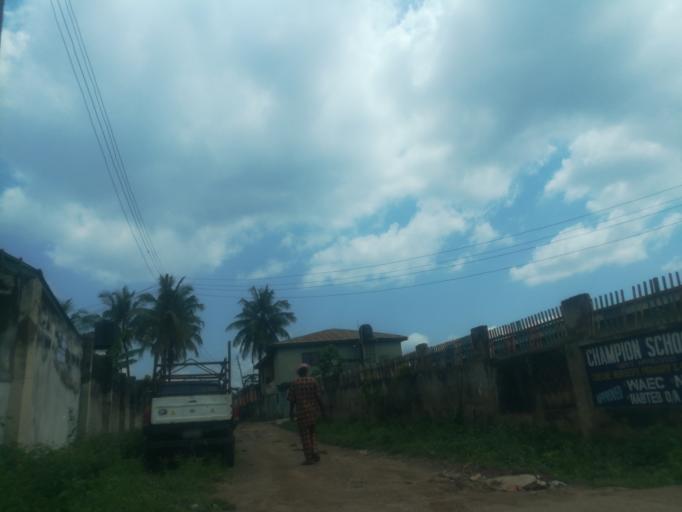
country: NG
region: Oyo
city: Ibadan
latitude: 7.3934
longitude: 3.9651
